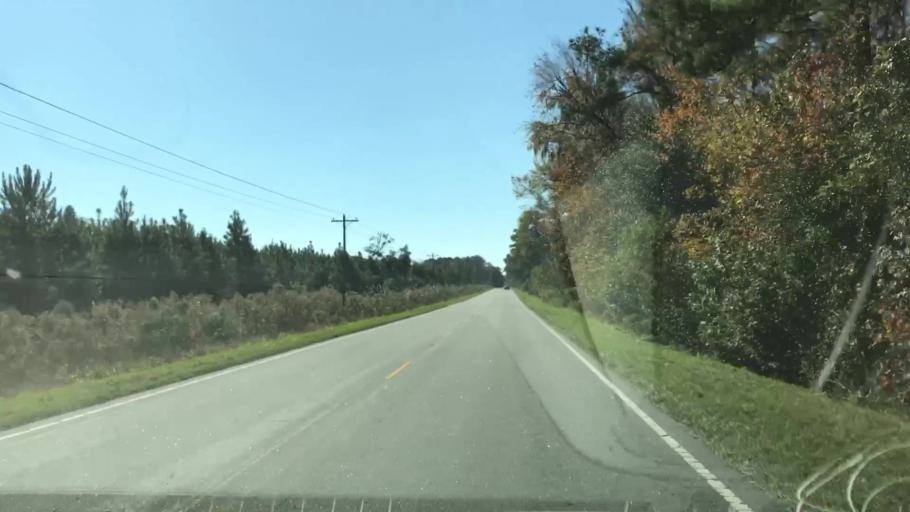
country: US
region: South Carolina
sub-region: Jasper County
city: Ridgeland
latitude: 32.4354
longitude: -80.8943
